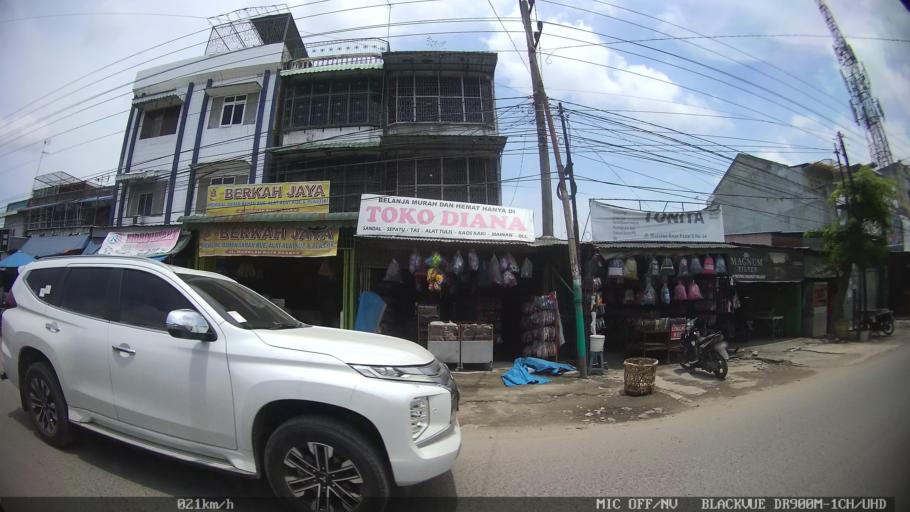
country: ID
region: North Sumatra
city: Labuhan Deli
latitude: 3.7083
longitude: 98.6600
